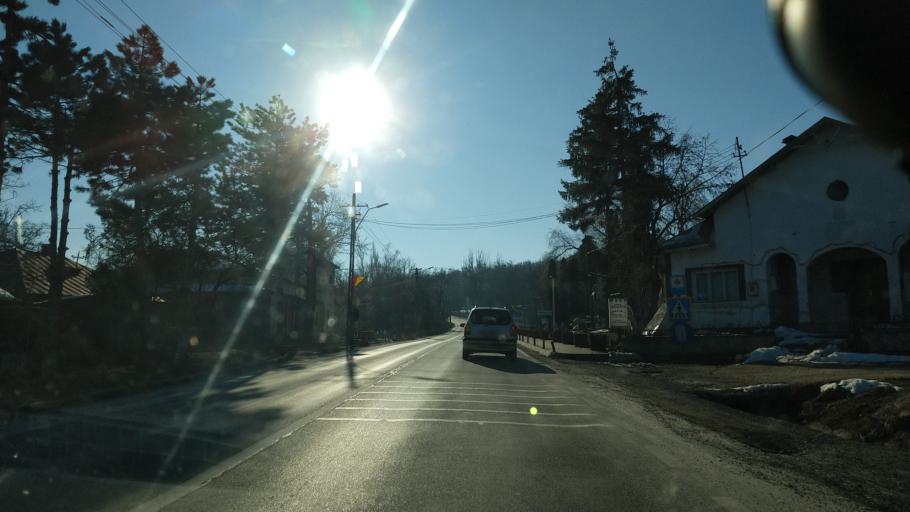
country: RO
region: Iasi
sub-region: Comuna Strunga
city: Strunga
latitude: 47.1683
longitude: 26.9531
